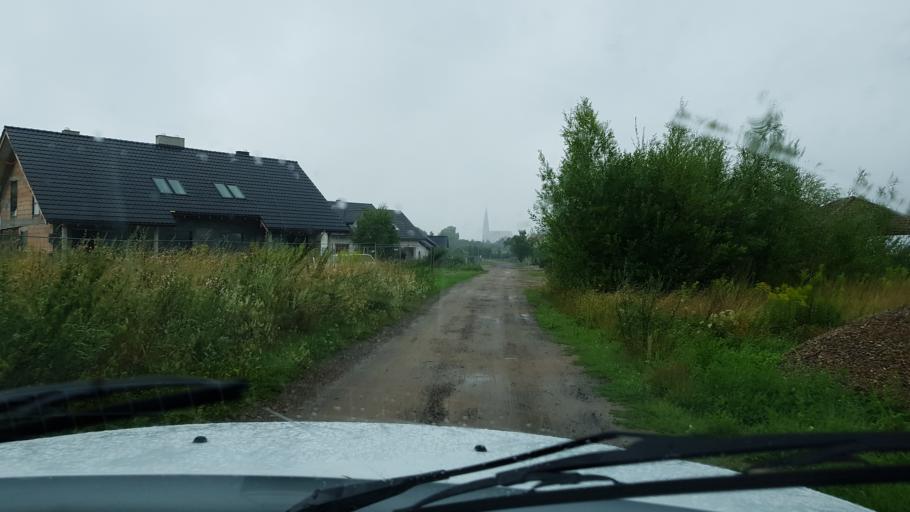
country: PL
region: West Pomeranian Voivodeship
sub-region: Powiat gryfinski
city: Chojna
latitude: 52.9507
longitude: 14.4254
